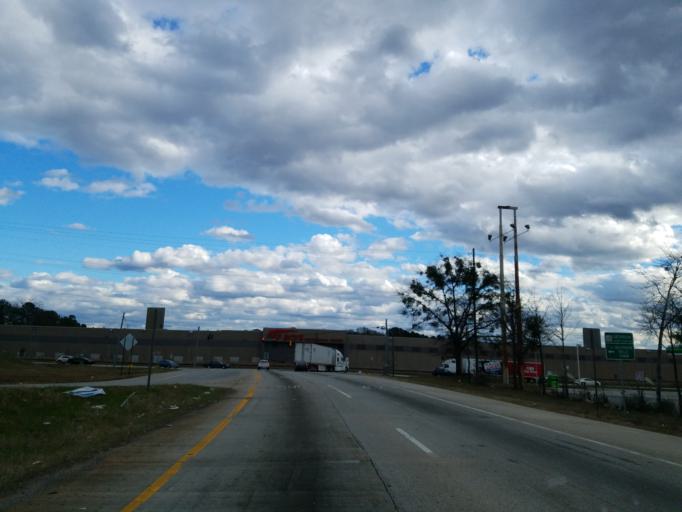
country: US
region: Georgia
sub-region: Henry County
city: McDonough
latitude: 33.4112
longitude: -84.1636
